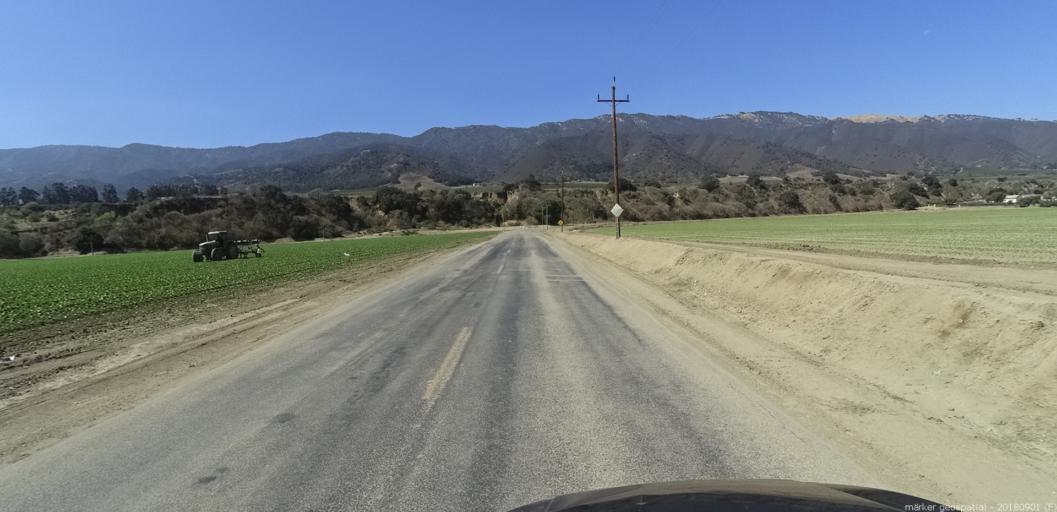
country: US
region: California
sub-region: Monterey County
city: Gonzales
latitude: 36.4792
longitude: -121.4775
